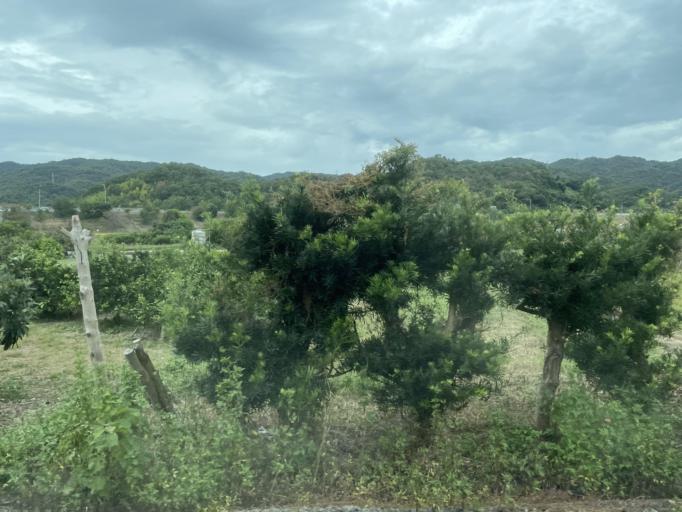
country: JP
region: Wakayama
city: Wakayama-shi
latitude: 34.2686
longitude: 135.2356
